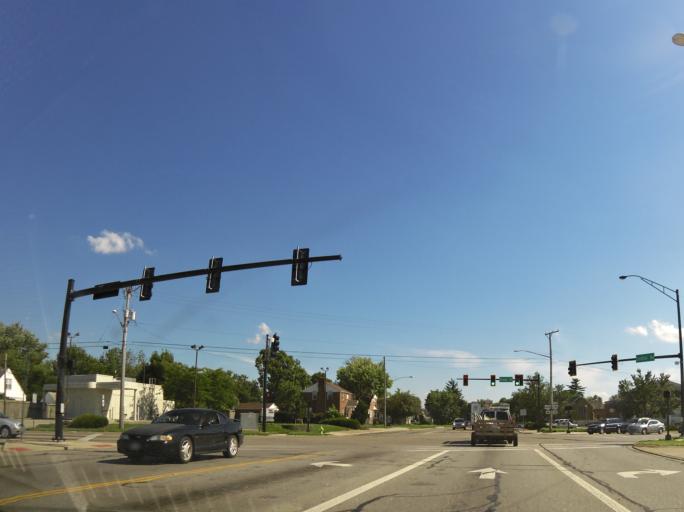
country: US
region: Ohio
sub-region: Greene County
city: Fairborn
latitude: 39.8324
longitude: -84.0192
